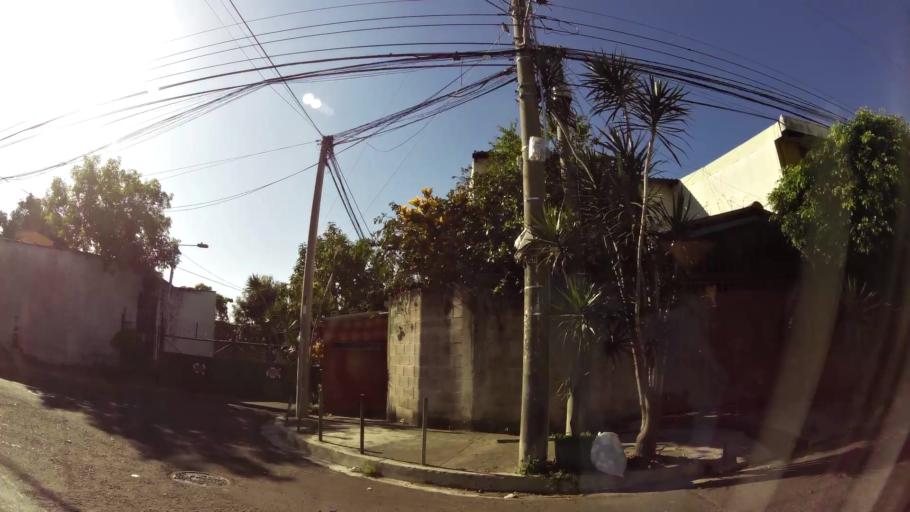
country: SV
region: La Libertad
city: Santa Tecla
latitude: 13.6903
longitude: -89.2927
